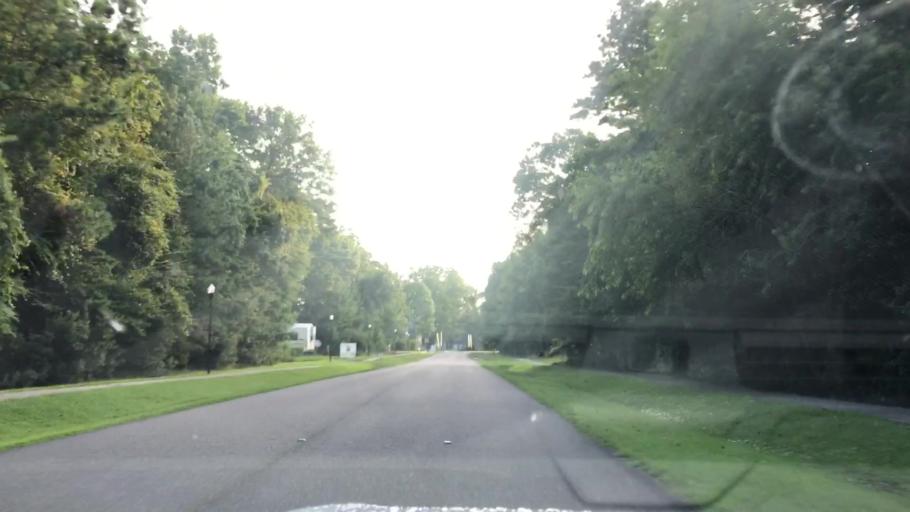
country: US
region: South Carolina
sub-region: Charleston County
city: Shell Point
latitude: 32.8401
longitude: -80.0929
